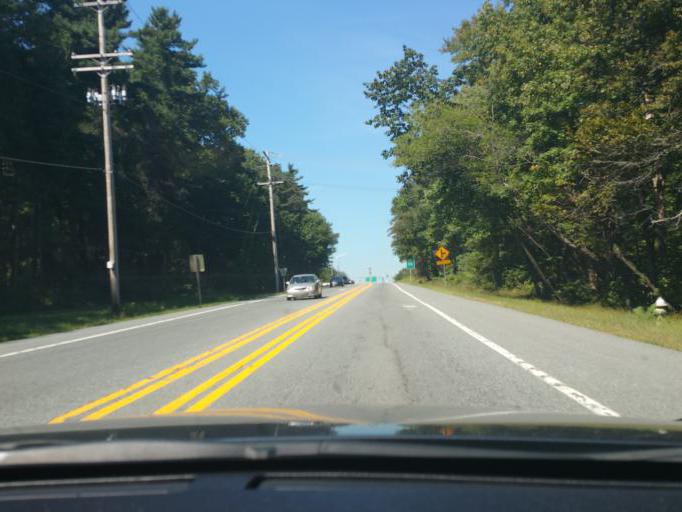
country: US
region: Maryland
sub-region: Harford County
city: Havre de Grace
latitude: 39.5661
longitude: -76.1272
